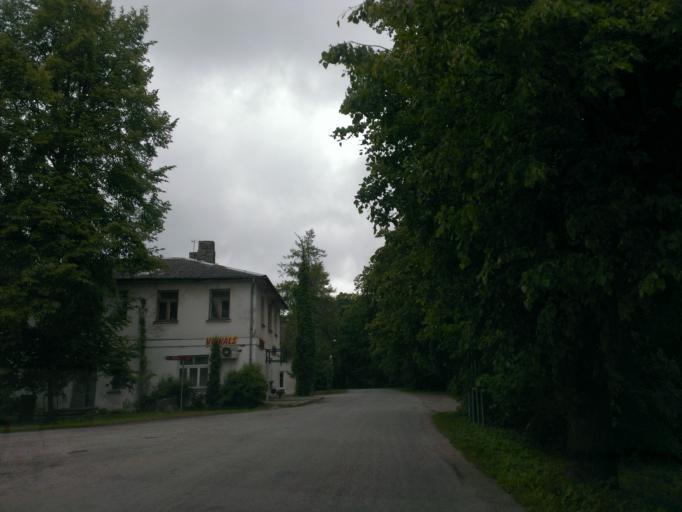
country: LV
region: Durbe
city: Liegi
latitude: 56.7341
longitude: 21.3872
